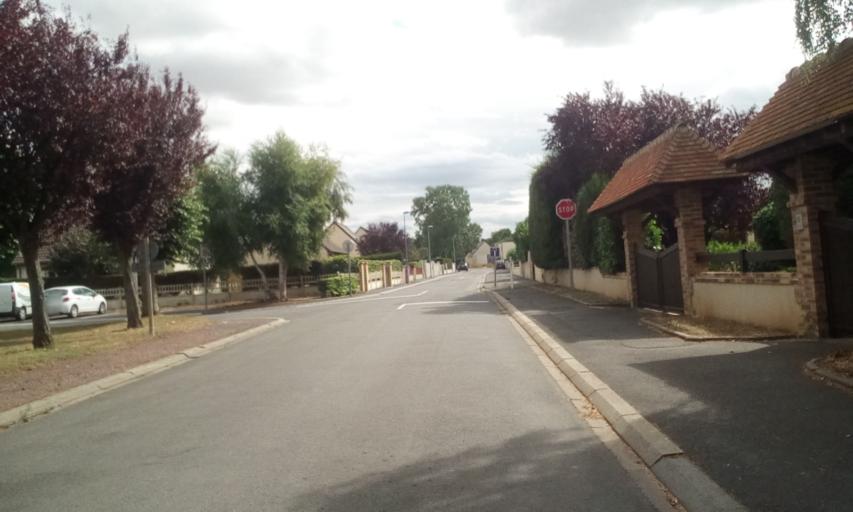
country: FR
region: Lower Normandy
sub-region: Departement du Calvados
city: Bellengreville
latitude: 49.1201
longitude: -0.2000
